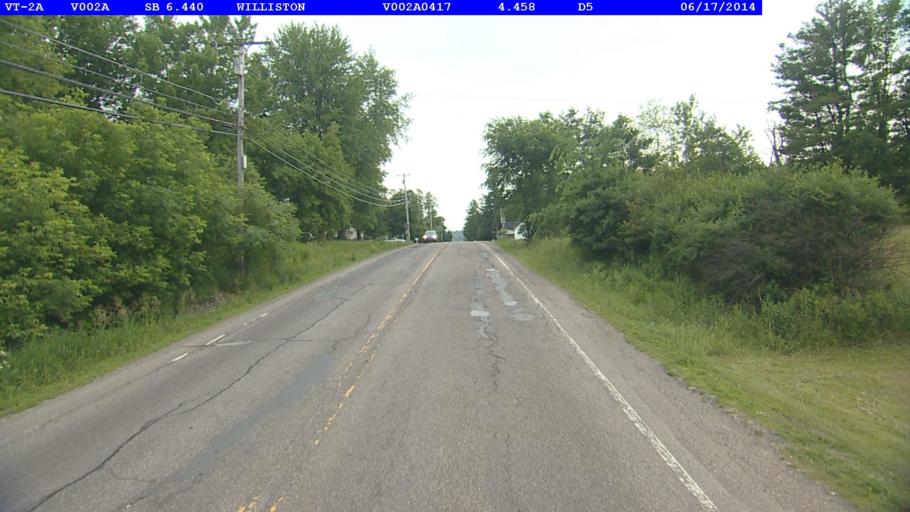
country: US
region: Vermont
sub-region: Chittenden County
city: Essex Junction
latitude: 44.4602
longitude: -73.1123
